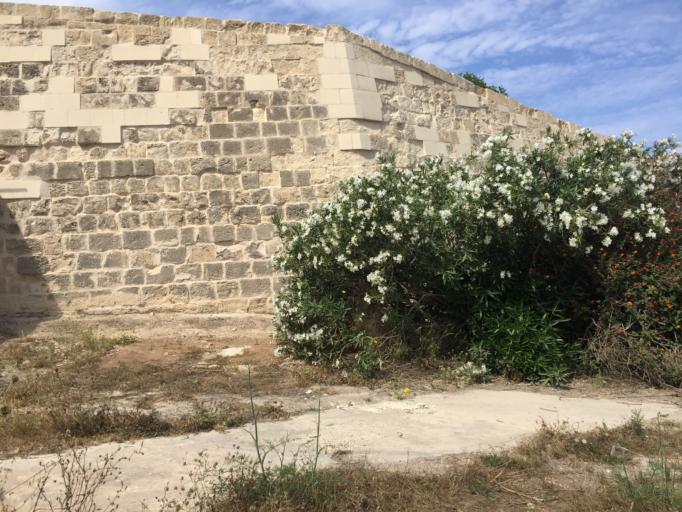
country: MT
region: Il-Furjana
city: Floriana
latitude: 35.9034
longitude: 14.5066
